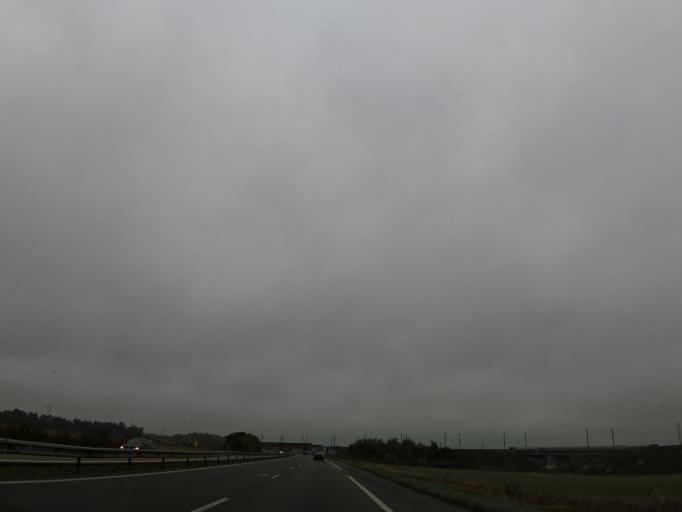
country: FR
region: Champagne-Ardenne
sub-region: Departement de la Marne
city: Verzy
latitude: 49.1092
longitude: 4.2540
